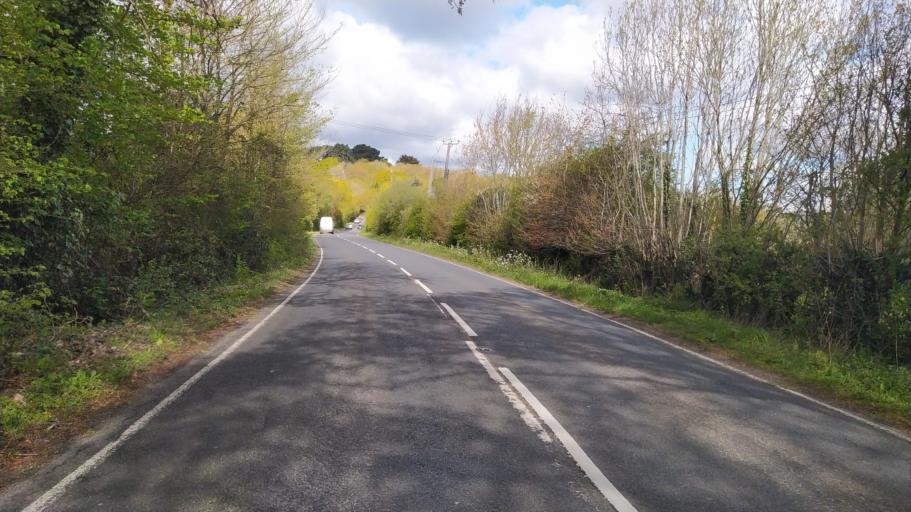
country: GB
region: England
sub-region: Hampshire
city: Hythe
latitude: 50.8731
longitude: -1.4249
